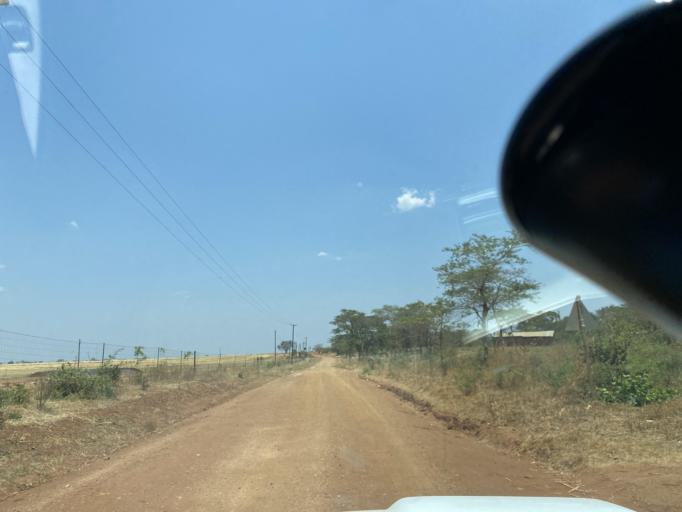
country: ZM
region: Lusaka
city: Lusaka
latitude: -15.4525
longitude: 28.0502
